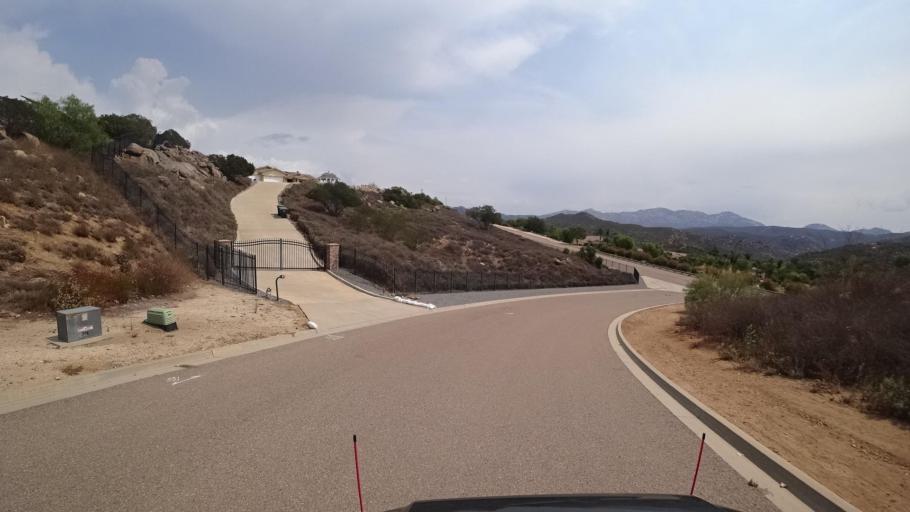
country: US
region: California
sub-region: San Diego County
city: Ramona
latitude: 32.9984
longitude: -116.8927
